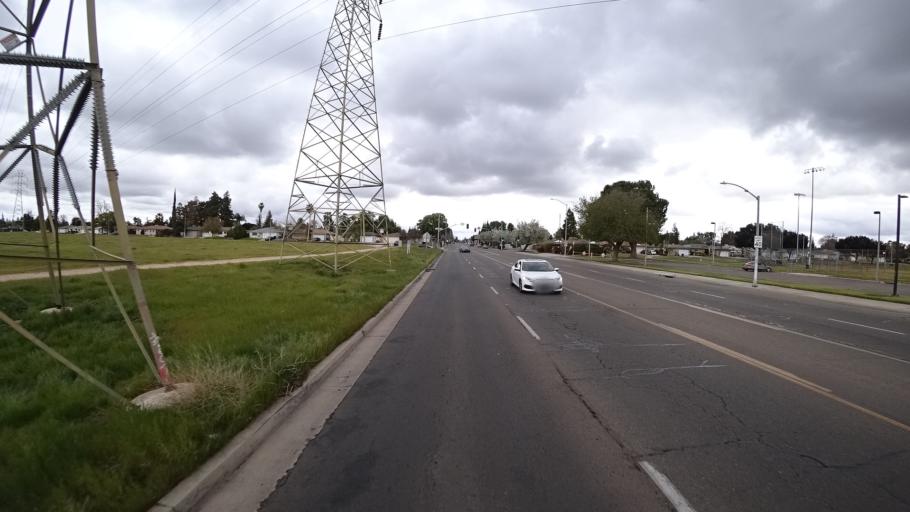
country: US
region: California
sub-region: Fresno County
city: Fresno
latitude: 36.8019
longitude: -119.8445
